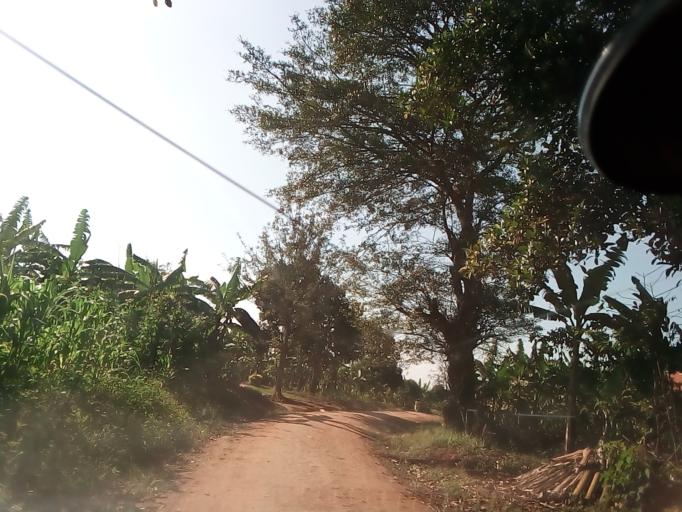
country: UG
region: Central Region
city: Masaka
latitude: -0.2688
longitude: 31.7217
